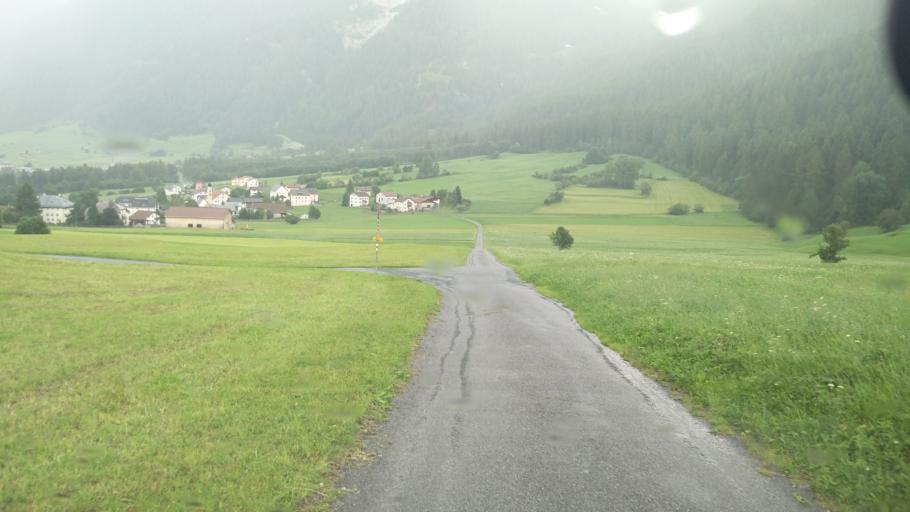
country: IT
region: Trentino-Alto Adige
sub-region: Bolzano
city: Tubre
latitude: 46.6003
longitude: 10.4000
